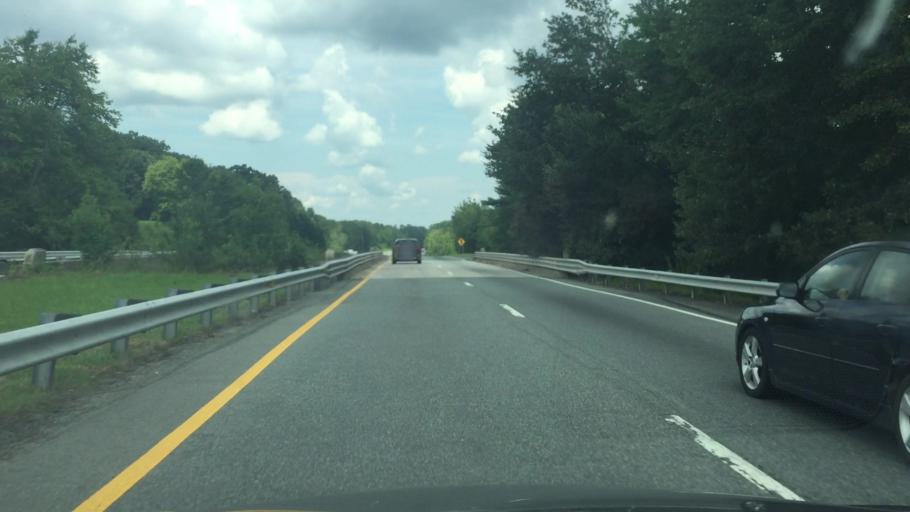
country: US
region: North Carolina
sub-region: Randolph County
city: Asheboro
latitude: 35.6201
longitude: -79.8254
